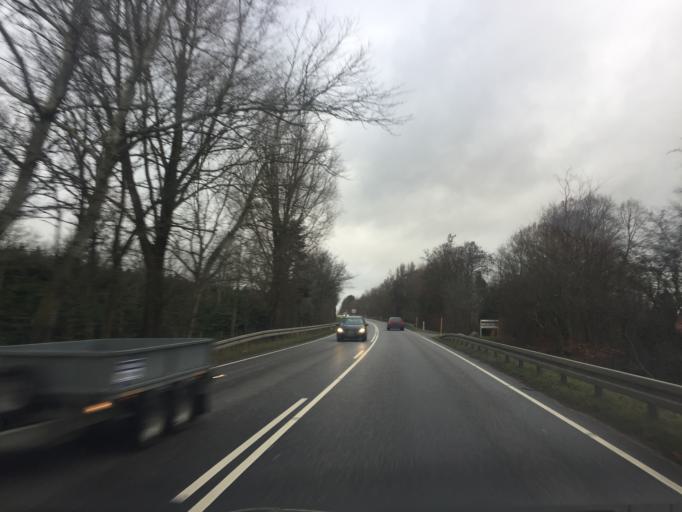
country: DK
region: Zealand
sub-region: Soro Kommune
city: Stenlille
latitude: 55.5138
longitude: 11.5819
